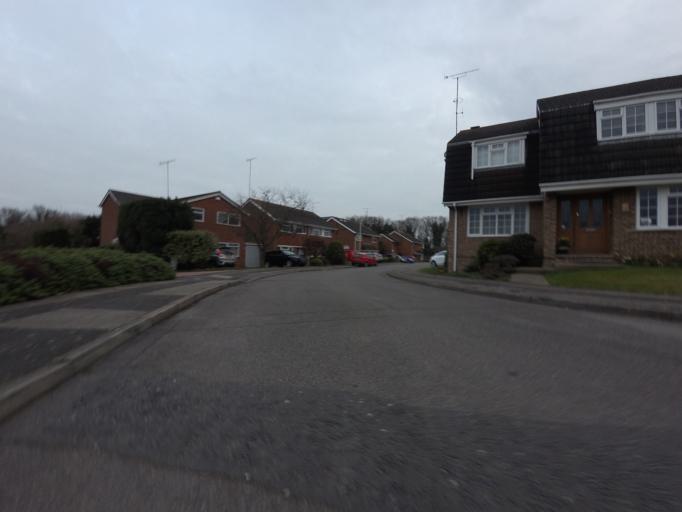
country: GB
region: England
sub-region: Kent
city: Swanley
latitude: 51.3990
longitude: 0.1835
